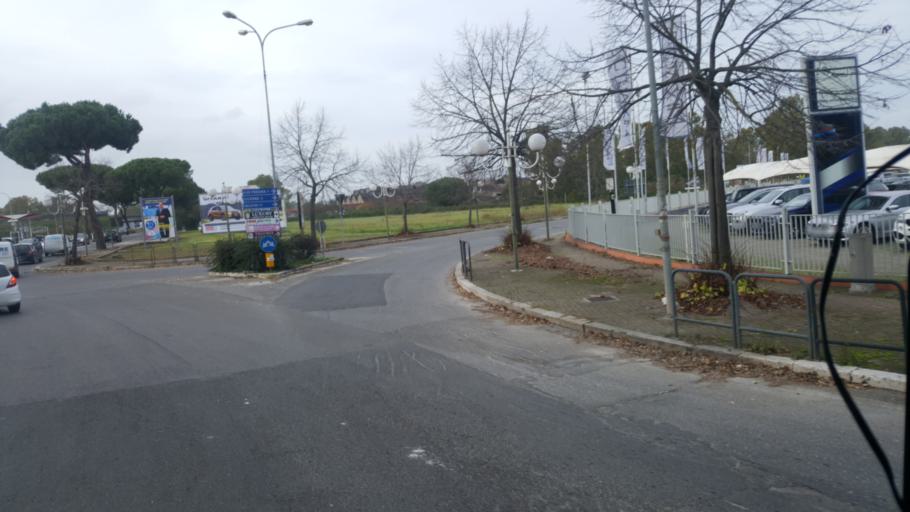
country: IT
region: Latium
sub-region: Provincia di Latina
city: Borgo Podgora
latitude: 41.4820
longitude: 12.8642
